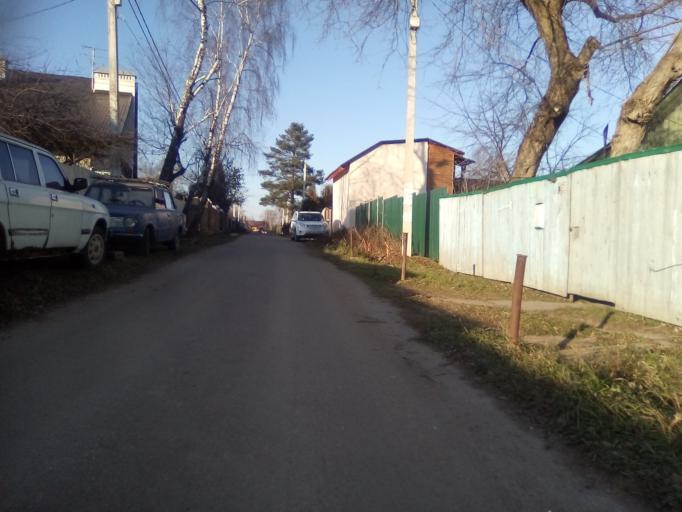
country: RU
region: Moskovskaya
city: Lesnoy Gorodok
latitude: 55.6575
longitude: 37.1894
